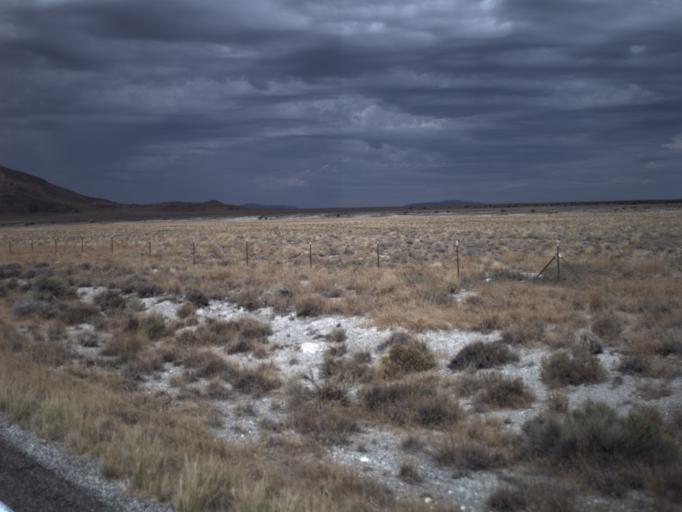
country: US
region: Utah
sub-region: Tooele County
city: Wendover
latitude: 41.4313
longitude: -113.7964
